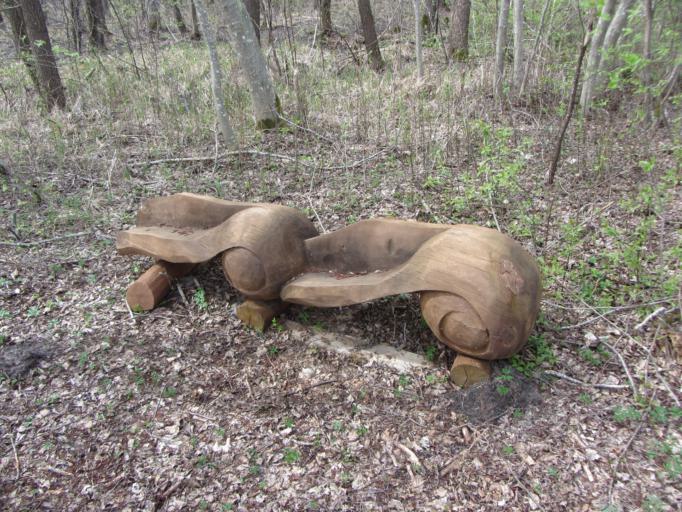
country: LT
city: Zarasai
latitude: 55.5802
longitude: 26.1549
